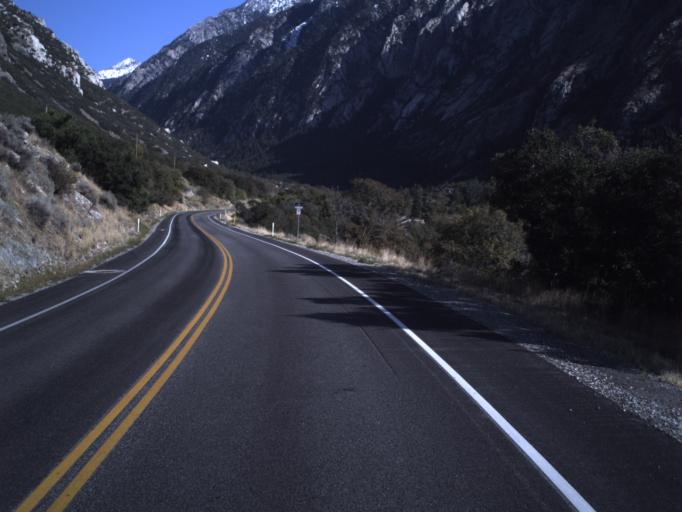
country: US
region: Utah
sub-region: Salt Lake County
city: Granite
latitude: 40.5768
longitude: -111.7881
